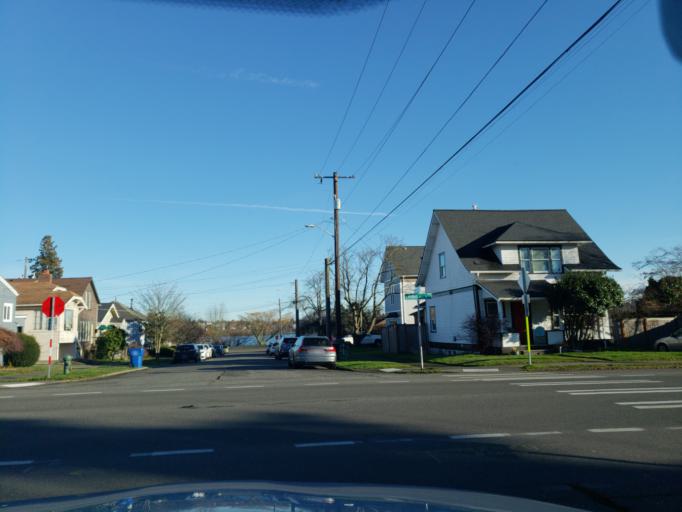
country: US
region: Washington
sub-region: King County
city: Seattle
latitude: 47.6778
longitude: -122.3474
